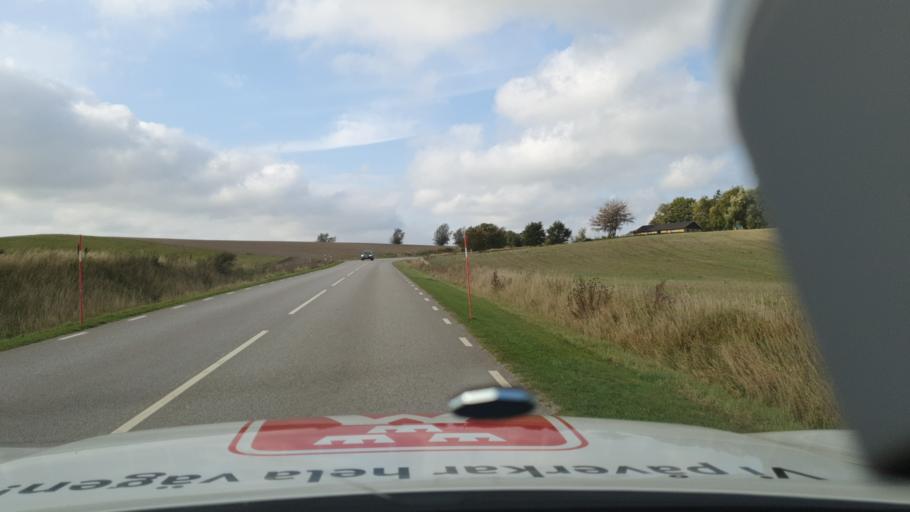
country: SE
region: Skane
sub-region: Svedala Kommun
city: Svedala
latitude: 55.4960
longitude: 13.1661
